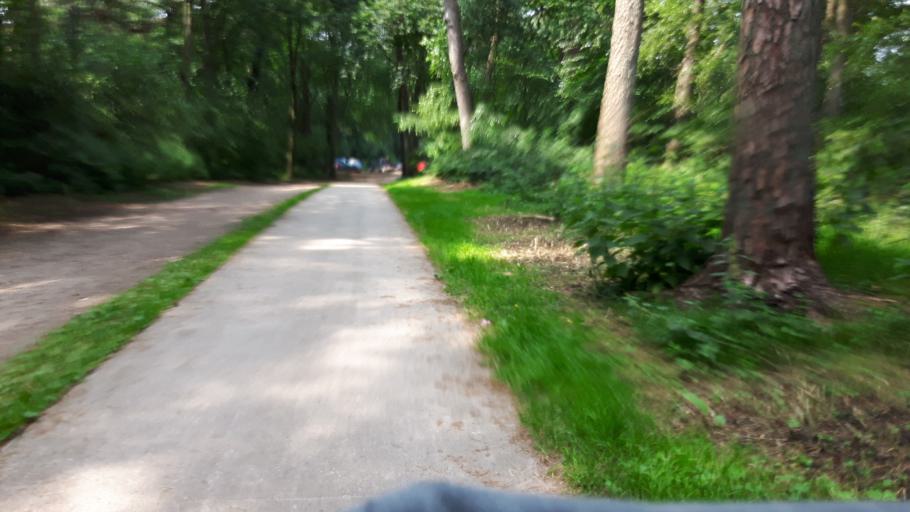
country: NL
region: Utrecht
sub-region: Gemeente Soest
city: Soest
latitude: 52.1548
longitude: 5.3014
